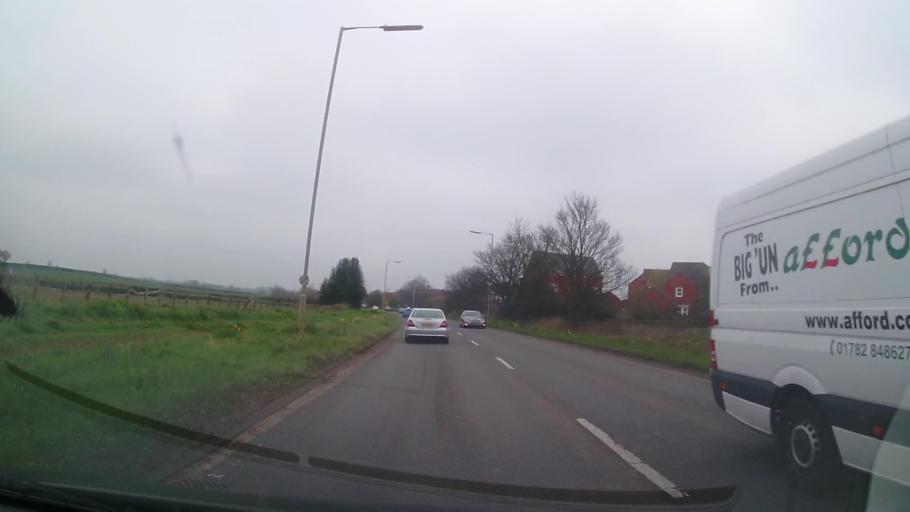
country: GB
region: England
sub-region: Shropshire
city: Market Drayton
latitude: 52.9030
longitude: -2.5068
